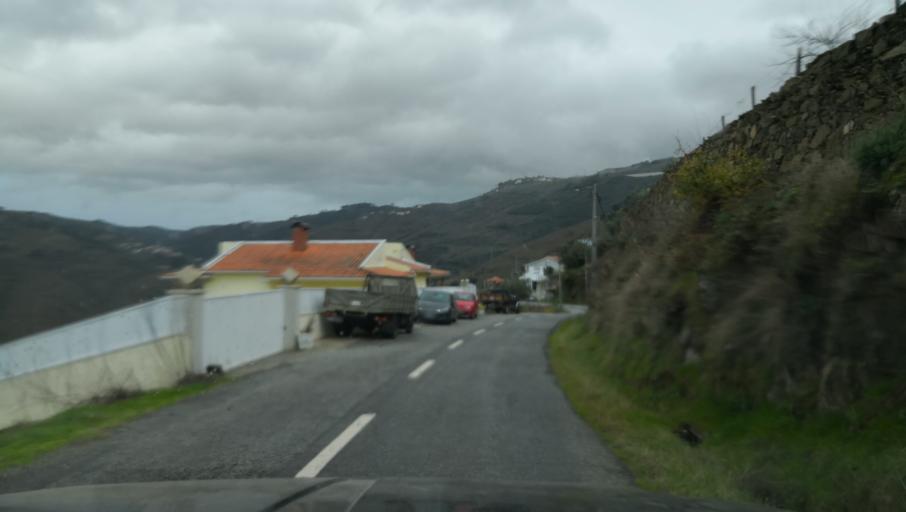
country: PT
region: Vila Real
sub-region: Santa Marta de Penaguiao
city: Santa Marta de Penaguiao
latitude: 41.2212
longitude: -7.7541
